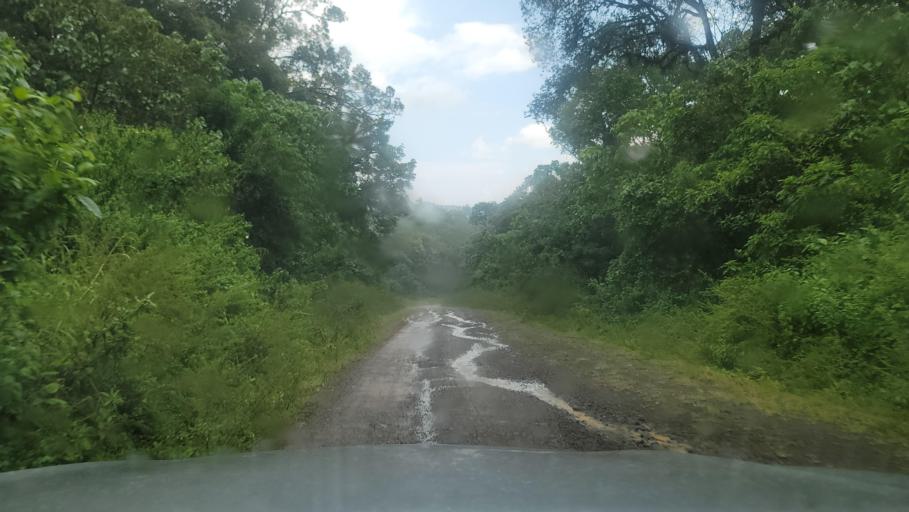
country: ET
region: Southern Nations, Nationalities, and People's Region
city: Bonga
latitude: 7.6626
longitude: 36.2461
